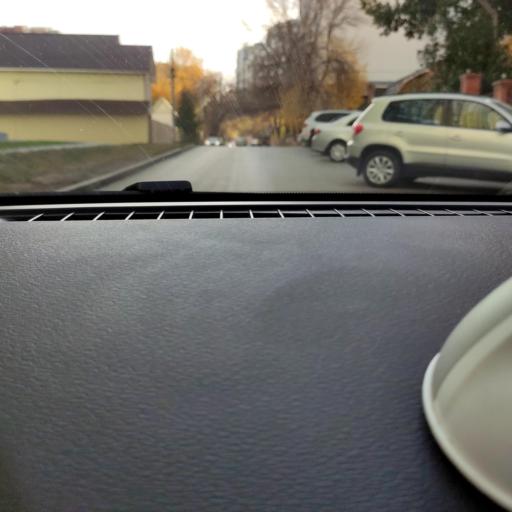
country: RU
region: Samara
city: Samara
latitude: 53.2254
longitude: 50.1517
